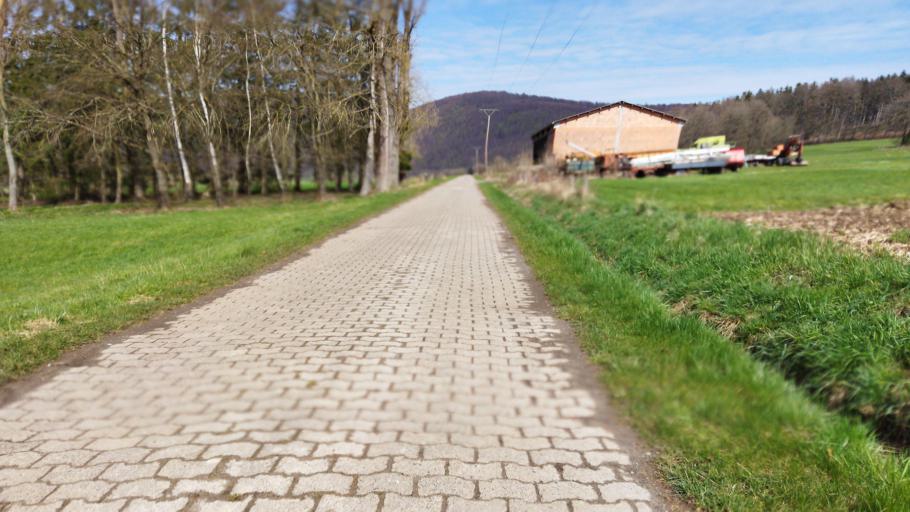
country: DE
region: Lower Saxony
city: Bad Karlshafen
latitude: 51.6416
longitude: 9.4979
